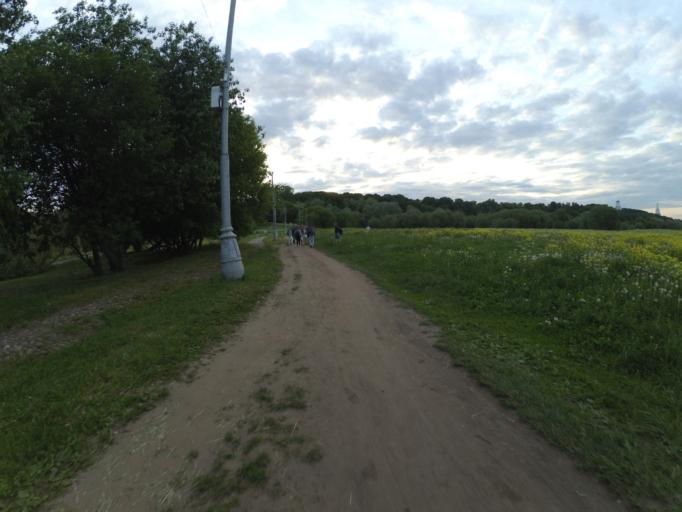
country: RU
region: Moscow
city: Kolomenskoye
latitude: 55.6570
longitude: 37.6692
